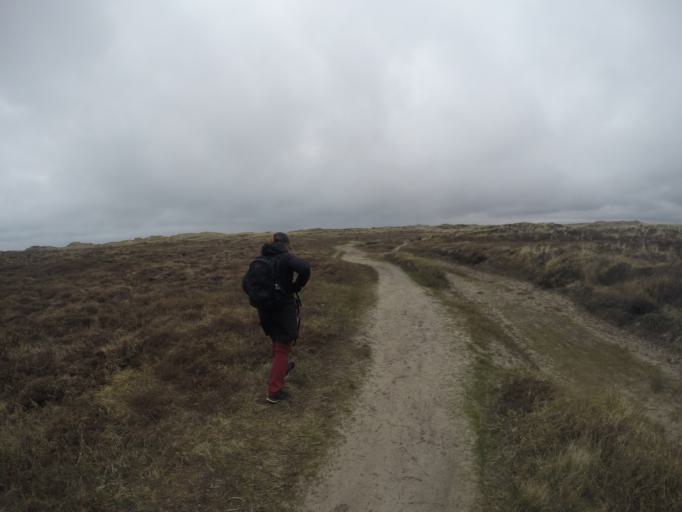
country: DK
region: Central Jutland
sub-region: Lemvig Kommune
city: Thyboron
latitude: 56.8274
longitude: 8.2631
